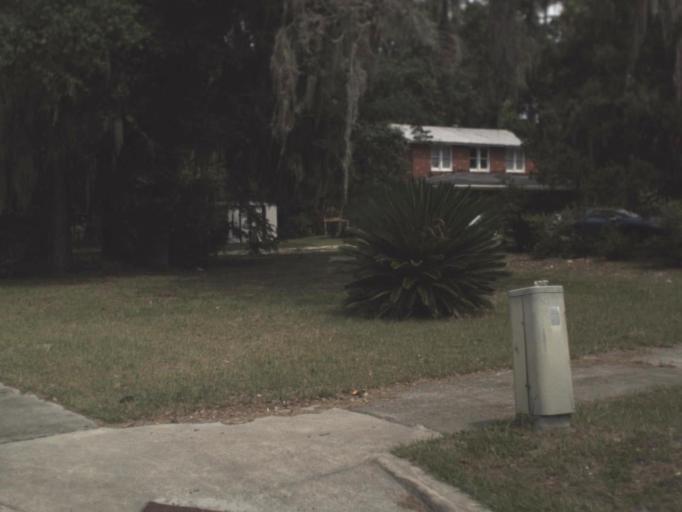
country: US
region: Florida
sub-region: Putnam County
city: Palatka
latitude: 29.6434
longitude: -81.6477
